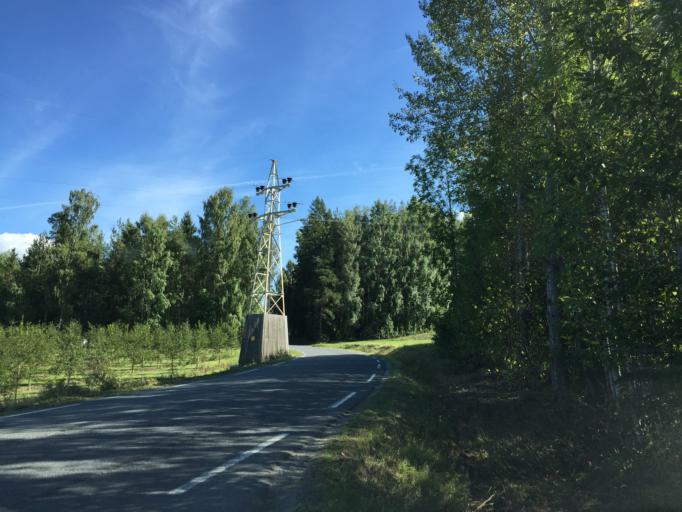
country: NO
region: Buskerud
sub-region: Ovre Eiker
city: Hokksund
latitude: 59.6946
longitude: 9.8413
